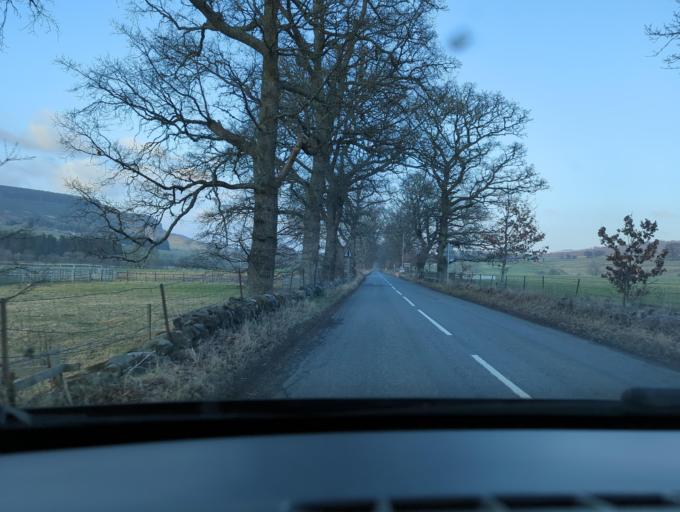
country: GB
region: Scotland
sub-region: Perth and Kinross
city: Methven
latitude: 56.5412
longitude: -3.6610
